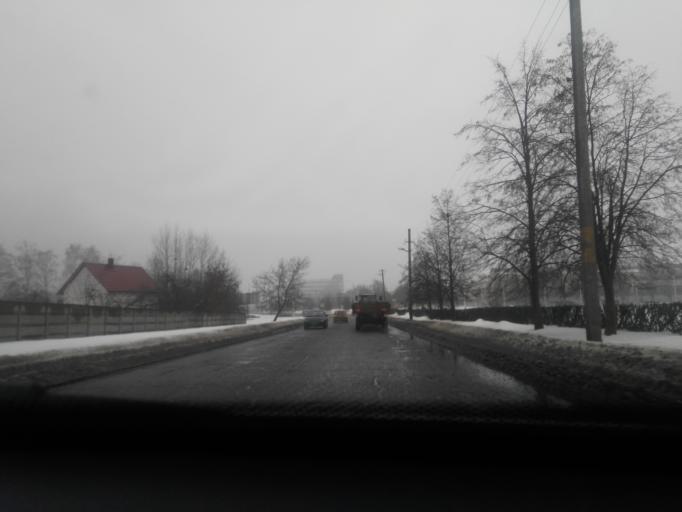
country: BY
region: Mogilev
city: Babruysk
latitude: 53.1852
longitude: 29.2140
